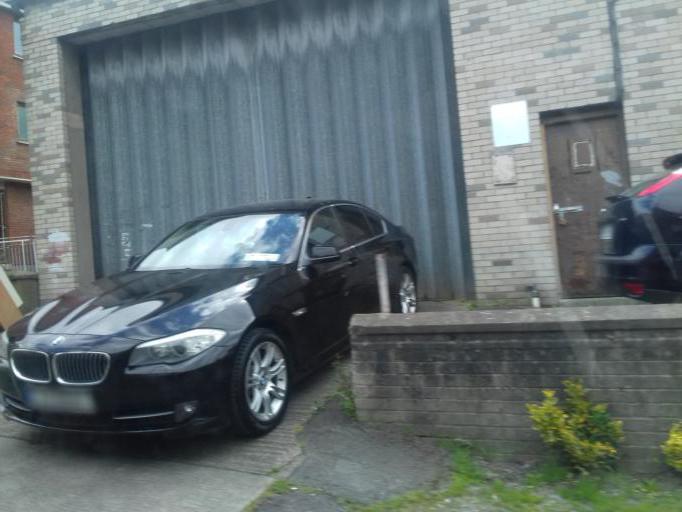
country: IE
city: Greenhills
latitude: 53.3414
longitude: -6.3045
